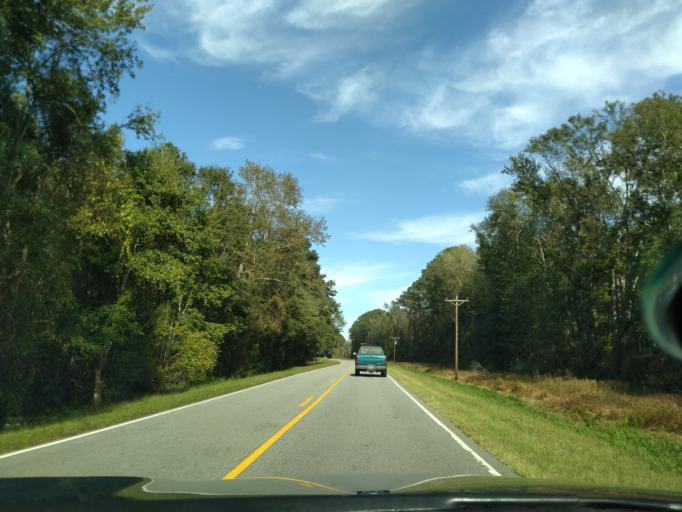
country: US
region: North Carolina
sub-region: Beaufort County
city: Belhaven
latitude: 35.6286
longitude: -76.6202
